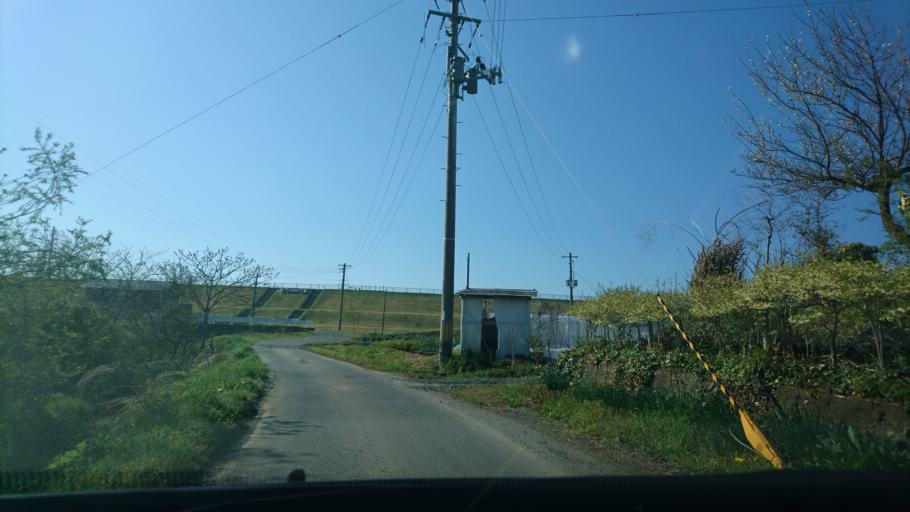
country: JP
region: Iwate
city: Ichinoseki
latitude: 38.9875
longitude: 141.1198
